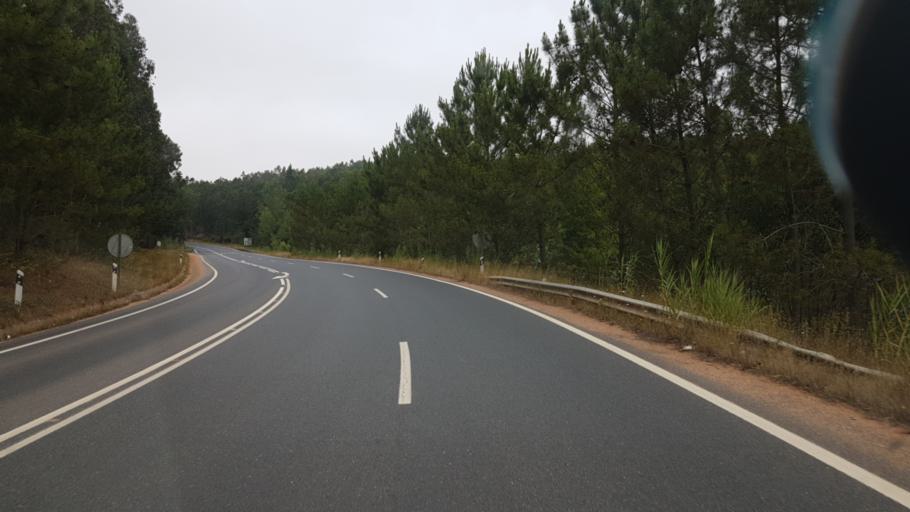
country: PT
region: Lisbon
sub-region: Torres Vedras
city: Torres Vedras
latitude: 39.1668
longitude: -9.2058
